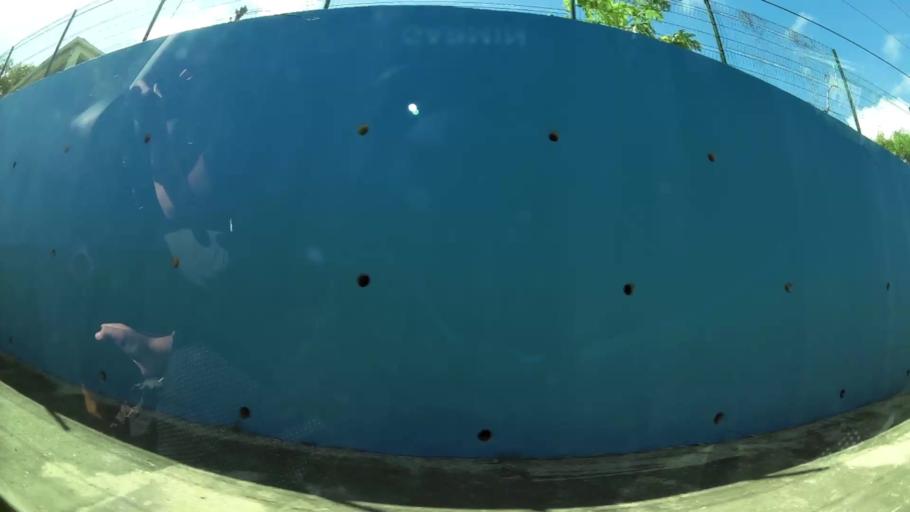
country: GP
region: Guadeloupe
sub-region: Guadeloupe
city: Petit-Canal
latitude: 16.3998
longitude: -61.4644
